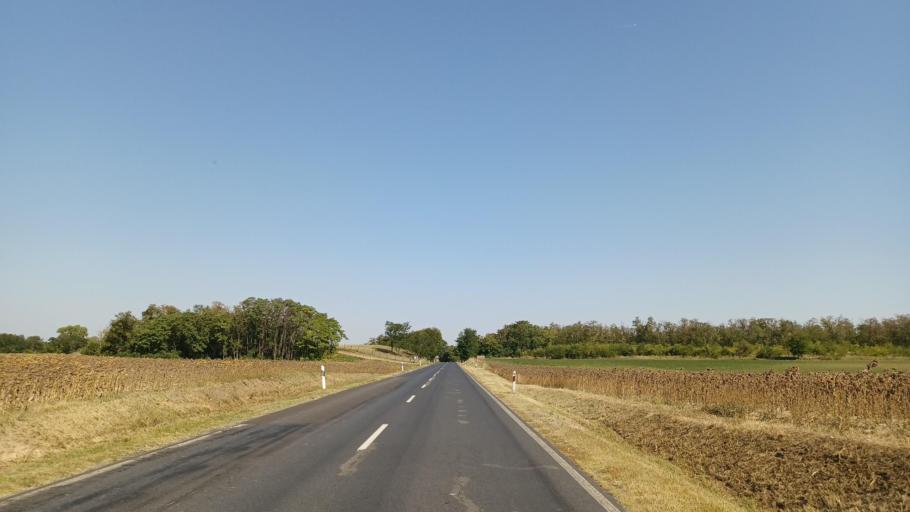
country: HU
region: Tolna
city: Nagydorog
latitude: 46.6552
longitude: 18.6514
